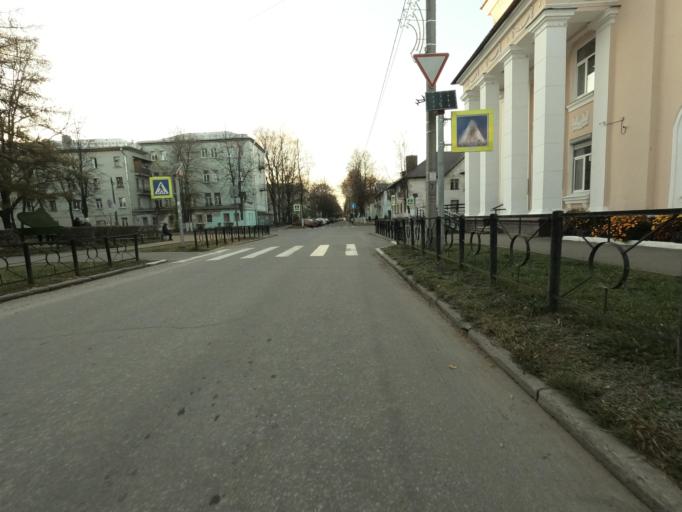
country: RU
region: Leningrad
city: Kirovsk
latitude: 59.8733
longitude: 30.9909
